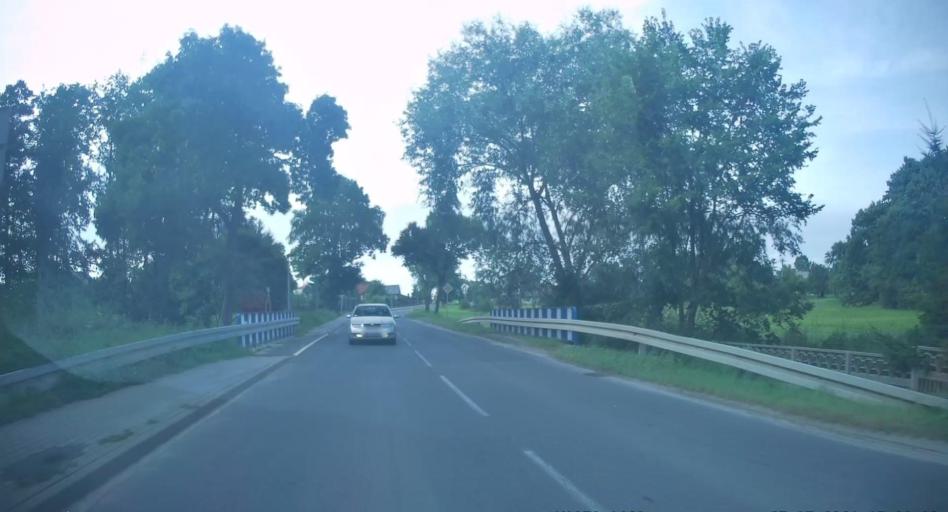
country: PL
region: Lodz Voivodeship
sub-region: Powiat tomaszowski
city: Rzeczyca
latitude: 51.5988
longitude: 20.2944
